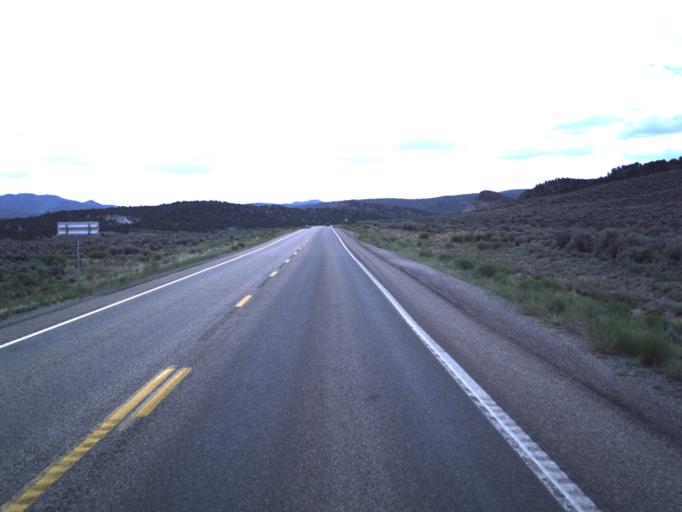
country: US
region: Utah
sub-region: Garfield County
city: Panguitch
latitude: 37.9656
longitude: -112.4169
